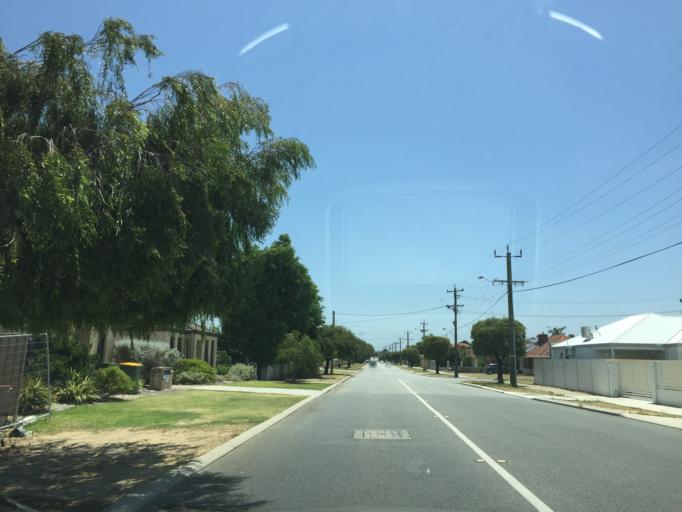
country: AU
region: Western Australia
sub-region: Canning
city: Queens Park
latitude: -32.0086
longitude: 115.9417
